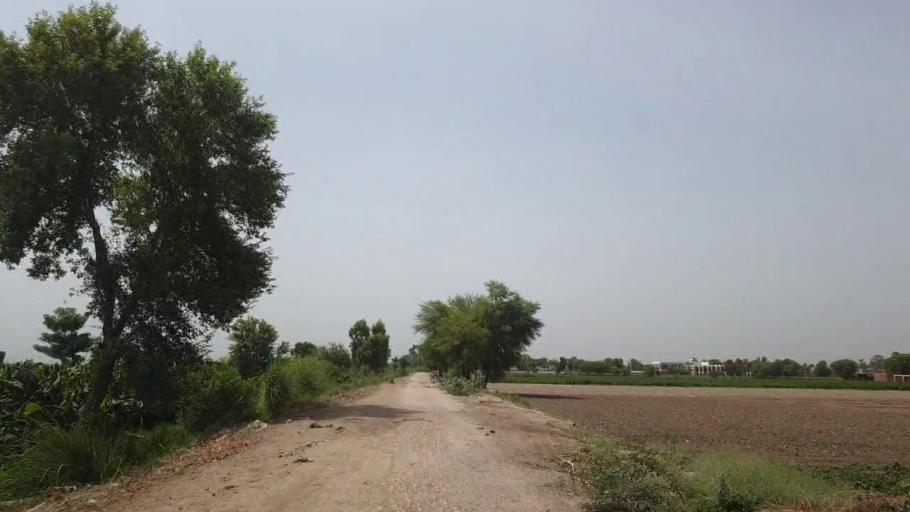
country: PK
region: Sindh
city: Sakrand
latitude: 26.1307
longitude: 68.2865
